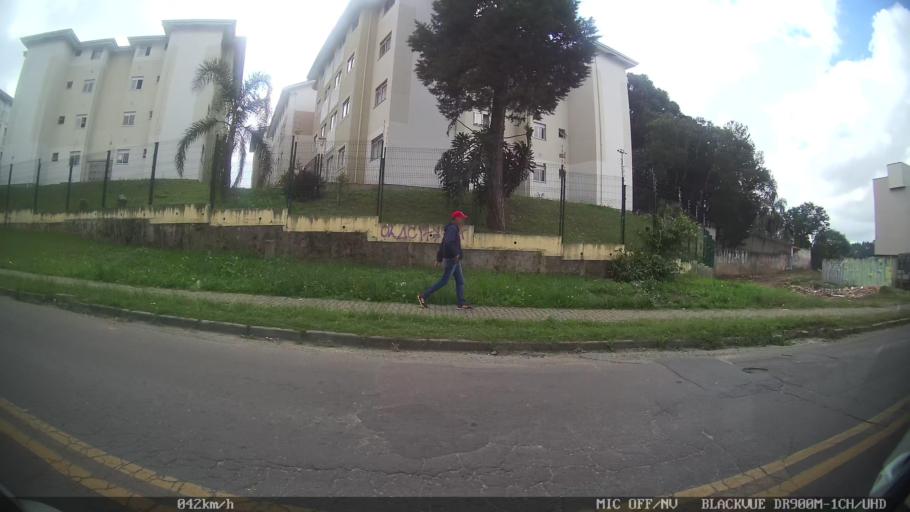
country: BR
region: Parana
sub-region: Pinhais
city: Pinhais
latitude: -25.3725
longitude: -49.2124
